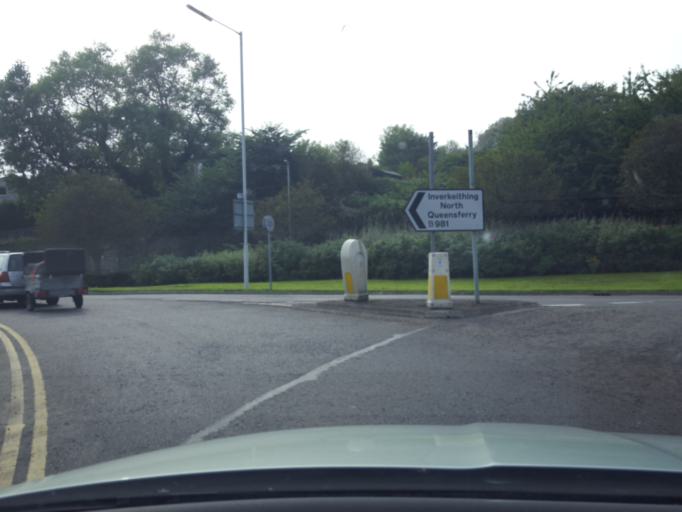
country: GB
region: Scotland
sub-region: Fife
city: Inverkeithing
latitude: 56.0366
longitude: -3.3960
